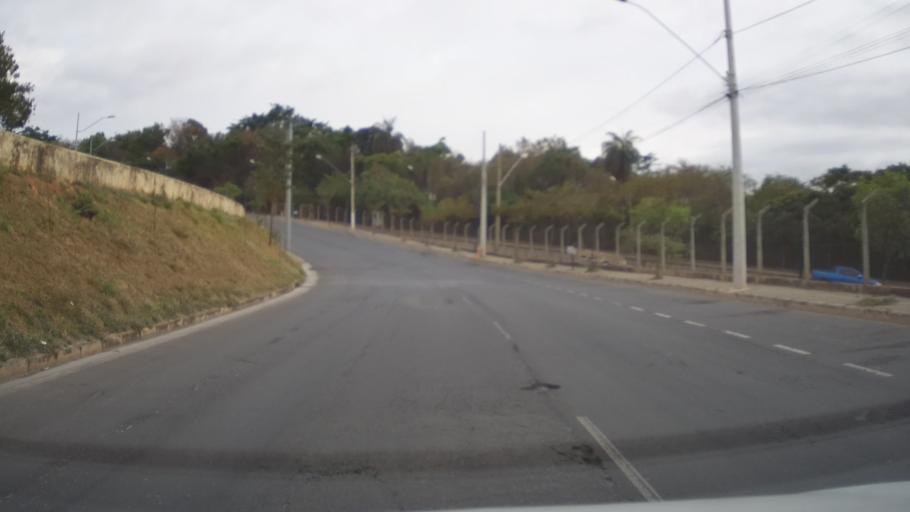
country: BR
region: Minas Gerais
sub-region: Belo Horizonte
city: Belo Horizonte
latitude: -19.8684
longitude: -43.9693
